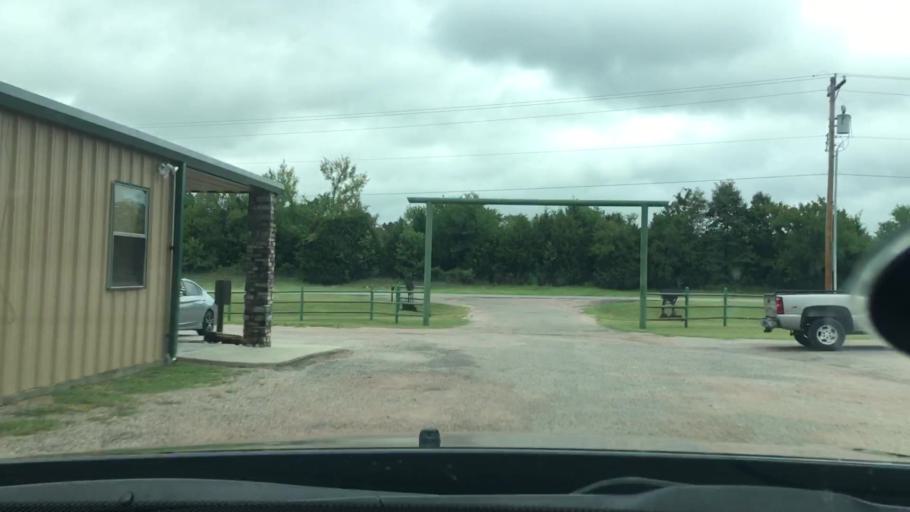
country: US
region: Oklahoma
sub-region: Johnston County
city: Tishomingo
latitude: 34.2297
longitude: -96.6523
